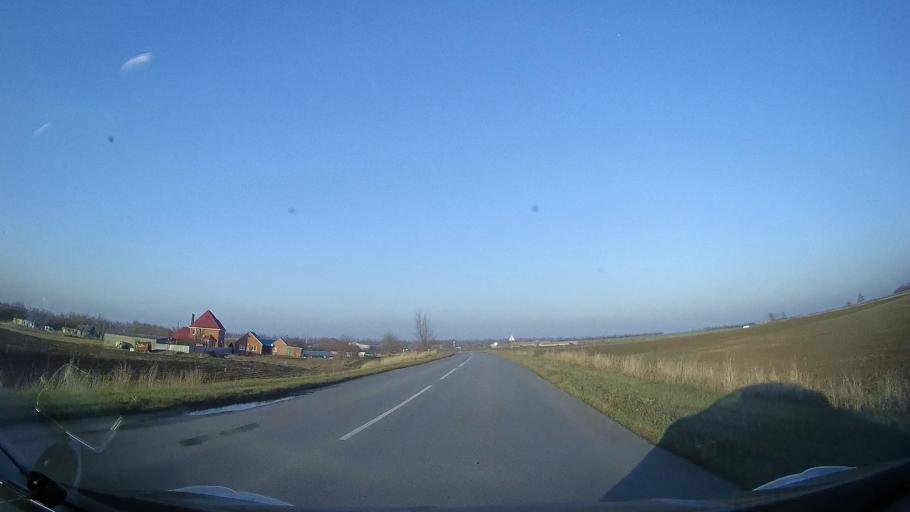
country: RU
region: Rostov
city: Kirovskaya
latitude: 47.0289
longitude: 39.9801
